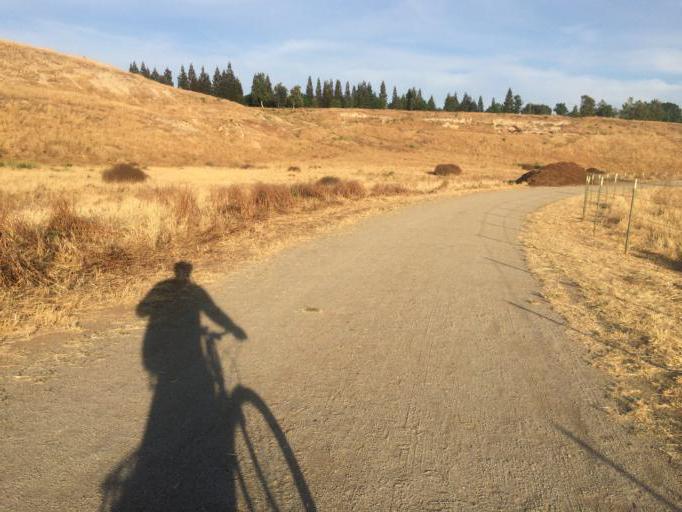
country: US
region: California
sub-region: Fresno County
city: Clovis
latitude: 36.8797
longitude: -119.7808
